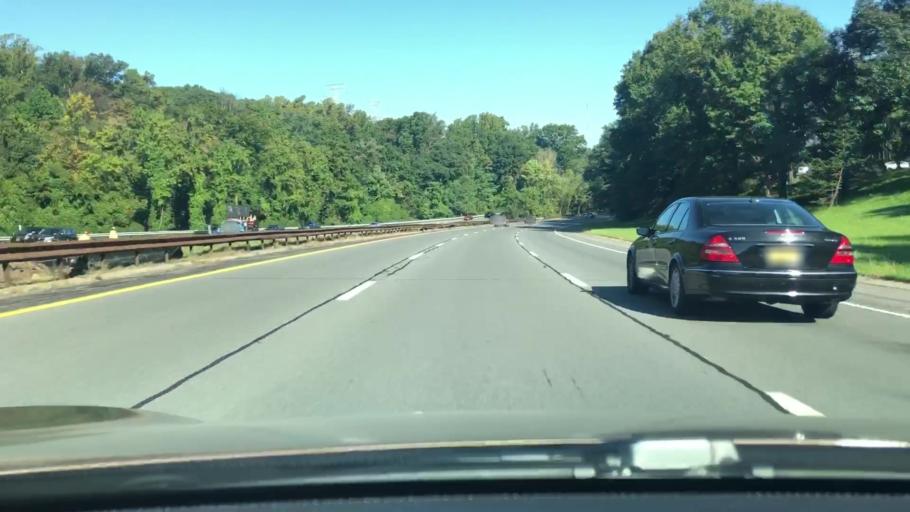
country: US
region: New York
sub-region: Westchester County
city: Ardsley
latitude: 41.0110
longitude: -73.8295
